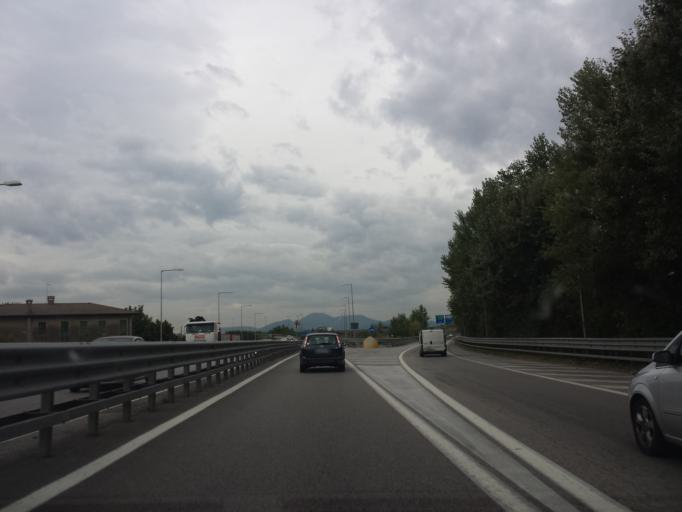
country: IT
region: Veneto
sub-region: Provincia di Padova
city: Mandriola-Sant'Agostino
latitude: 45.3847
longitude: 11.8330
